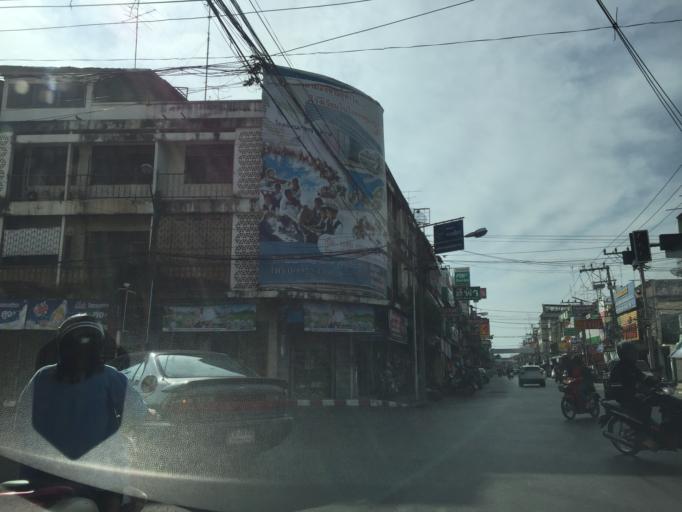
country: TH
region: Phitsanulok
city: Phitsanulok
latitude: 16.8201
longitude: 100.2650
